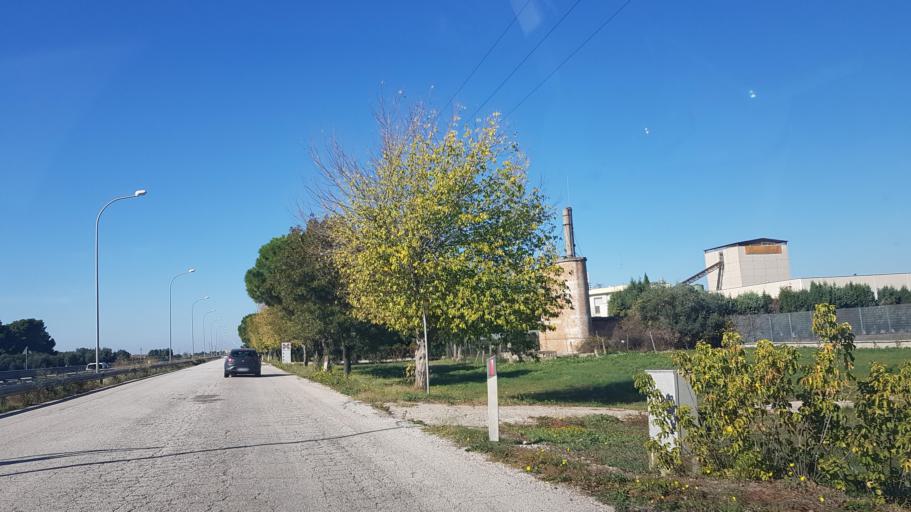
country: IT
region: Apulia
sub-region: Provincia di Foggia
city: Carapelle
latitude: 41.4033
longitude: 15.6483
